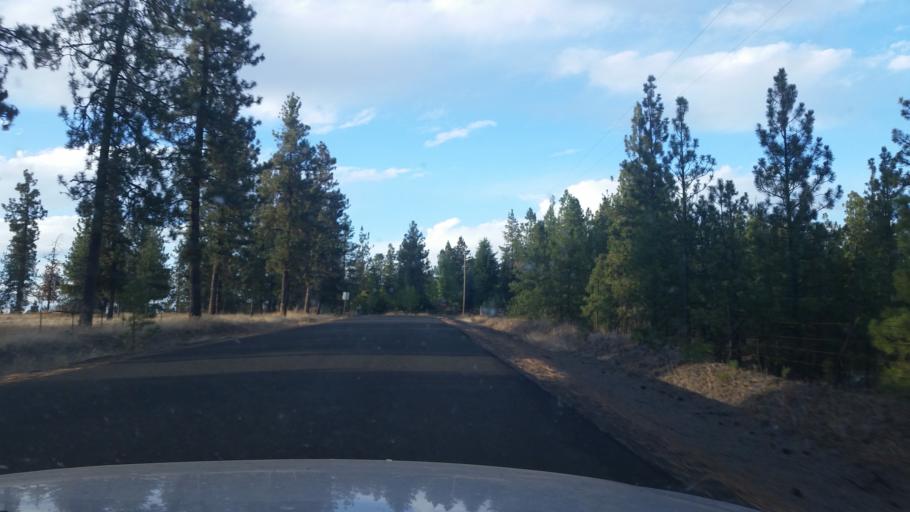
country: US
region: Washington
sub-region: Spokane County
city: Medical Lake
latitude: 47.4486
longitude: -117.7898
